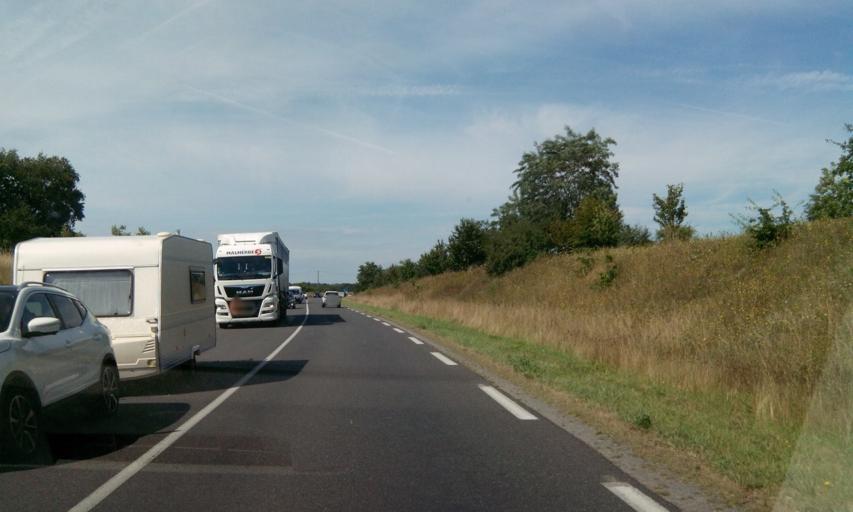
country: FR
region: Poitou-Charentes
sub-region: Departement de la Vienne
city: Charroux
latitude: 46.1544
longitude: 0.3800
